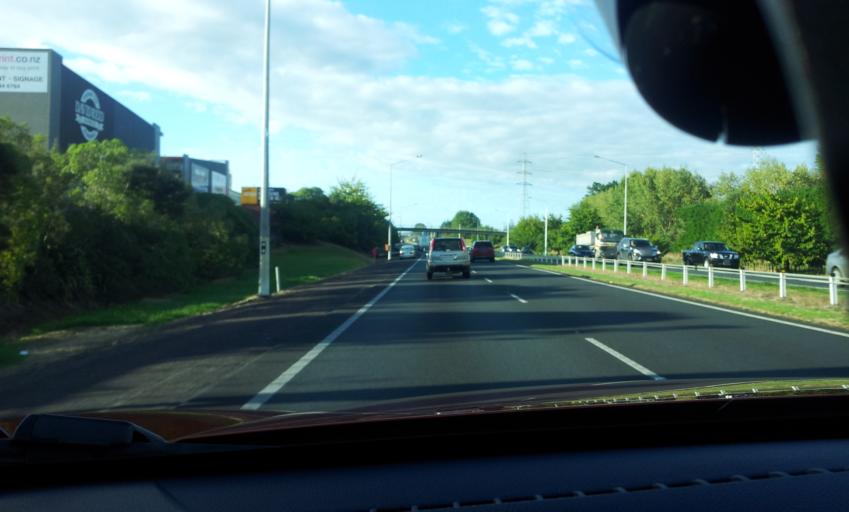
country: NZ
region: Auckland
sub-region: Auckland
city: Papakura
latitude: -37.1009
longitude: 174.9451
